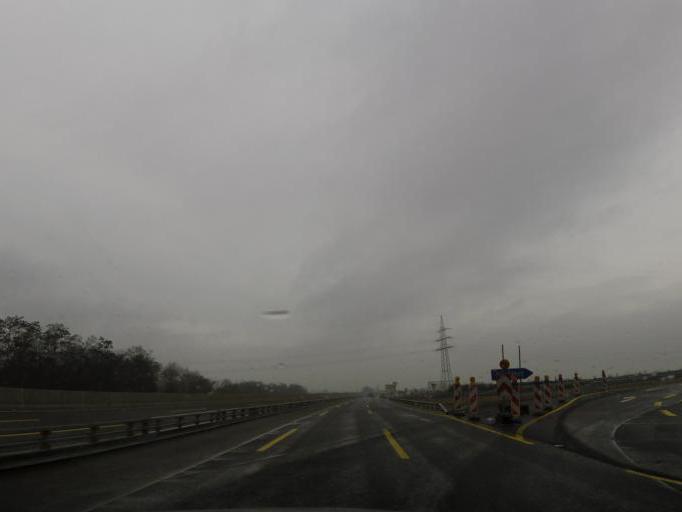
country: DE
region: Hesse
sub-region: Regierungsbezirk Giessen
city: Limburg an der Lahn
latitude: 50.3794
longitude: 8.0892
